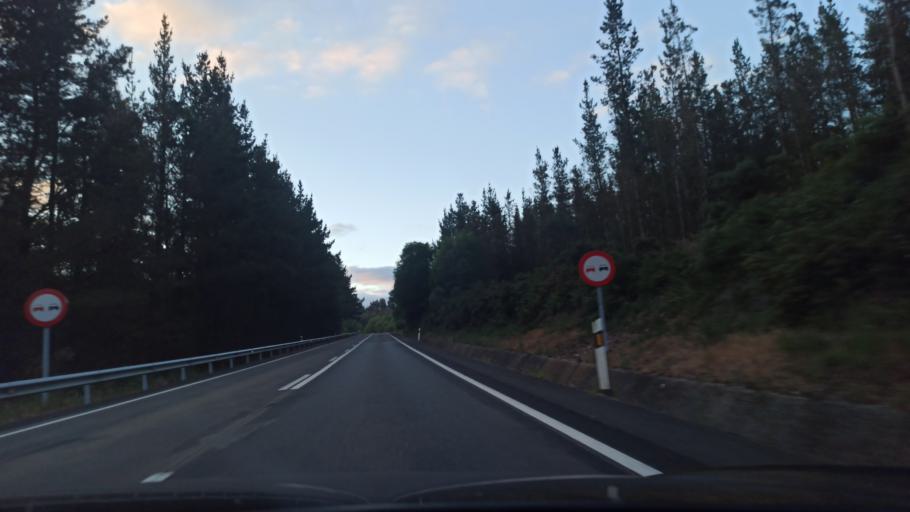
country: ES
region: Galicia
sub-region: Provincia de Lugo
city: Monterroso
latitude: 42.8211
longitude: -7.7623
